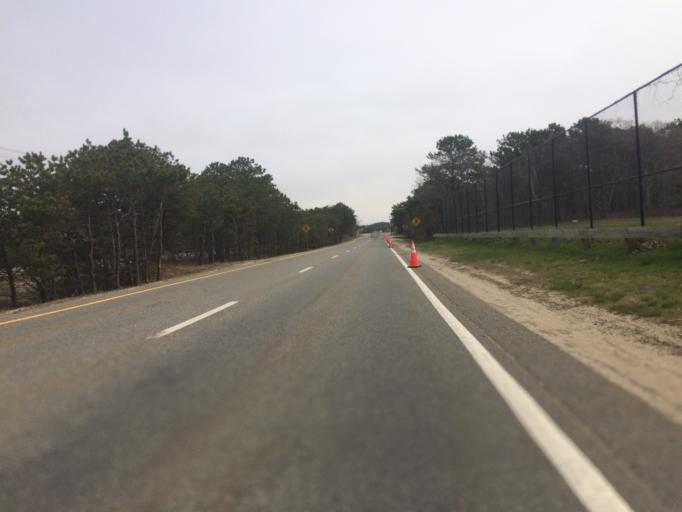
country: US
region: Massachusetts
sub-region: Barnstable County
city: Provincetown
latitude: 42.0569
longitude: -70.1922
